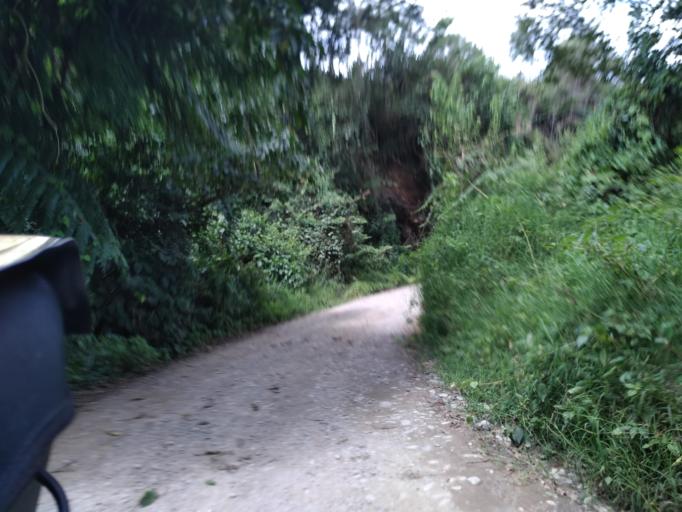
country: CO
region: Quindio
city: Salento
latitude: 4.6296
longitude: -75.5850
